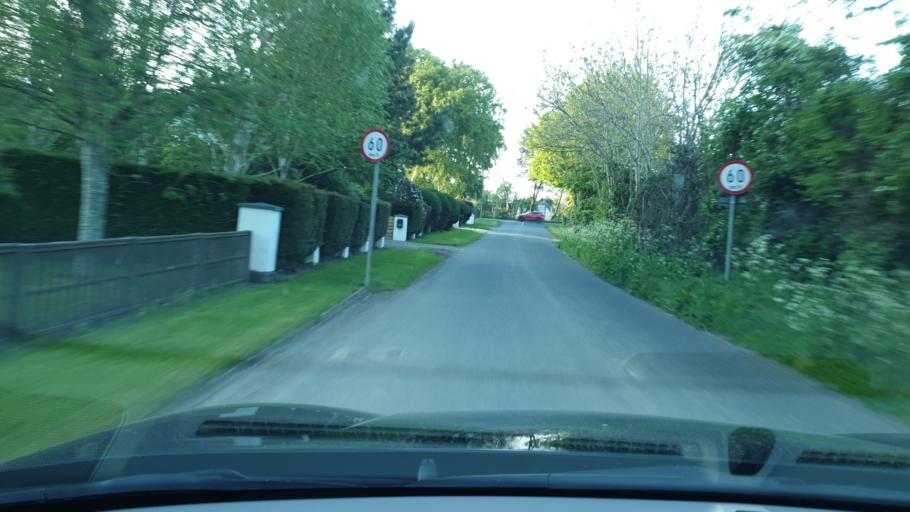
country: IE
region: Leinster
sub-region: An Mhi
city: Ashbourne
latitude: 53.4944
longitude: -6.3936
